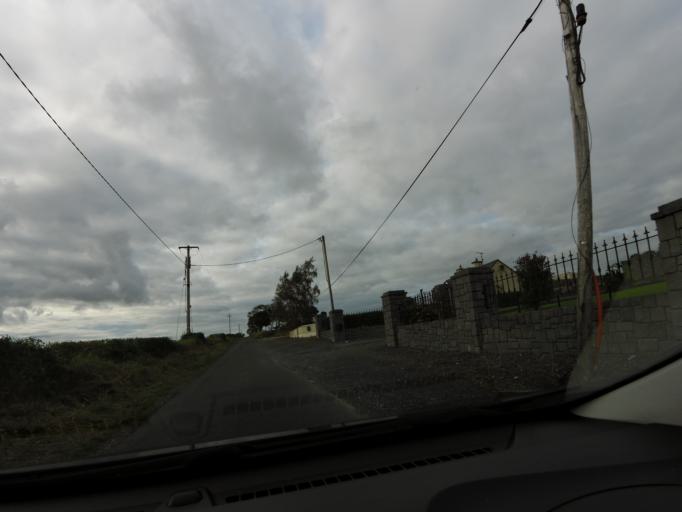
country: IE
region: Connaught
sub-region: County Galway
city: Ballinasloe
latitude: 53.3673
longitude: -8.1608
